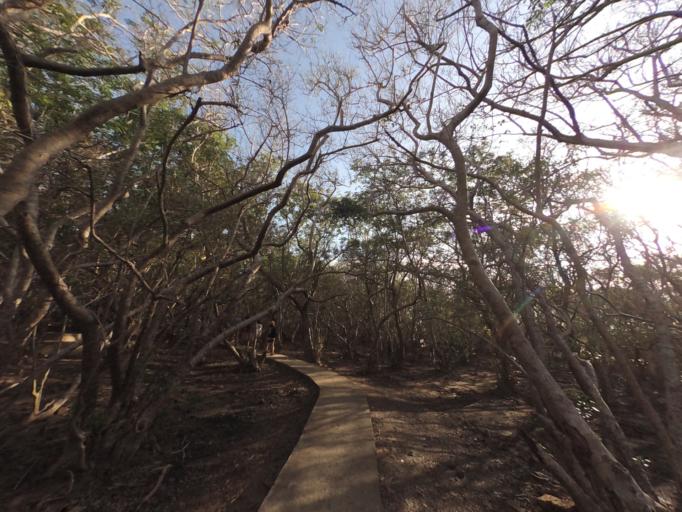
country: VN
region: Thua Thien-Hue
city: Hue
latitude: 16.5577
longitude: 107.6116
